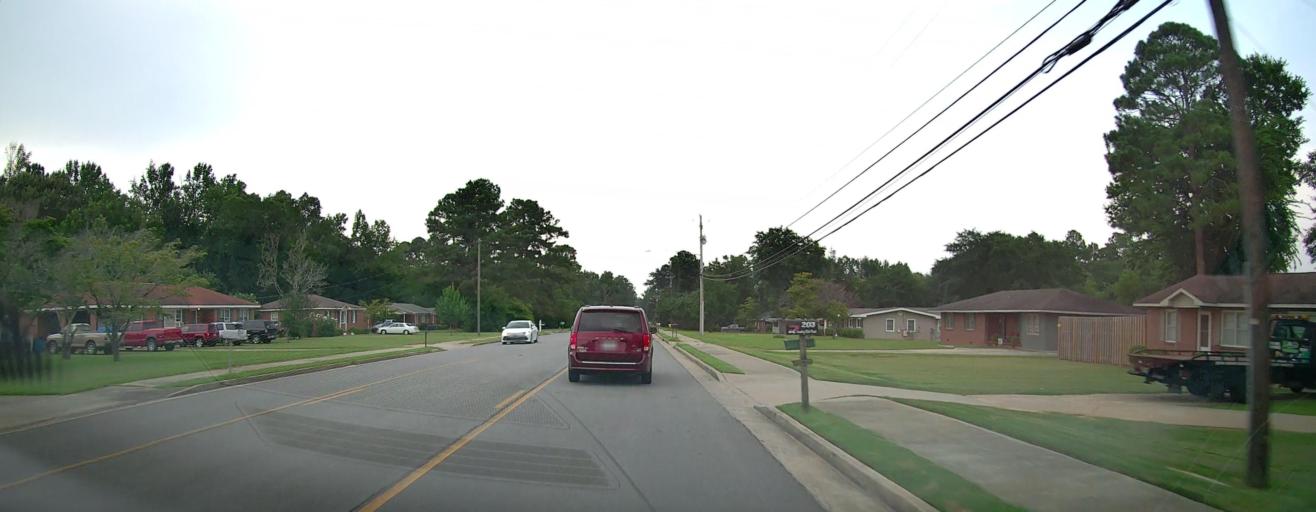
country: US
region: Georgia
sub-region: Laurens County
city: Dublin
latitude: 32.5635
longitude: -82.9125
